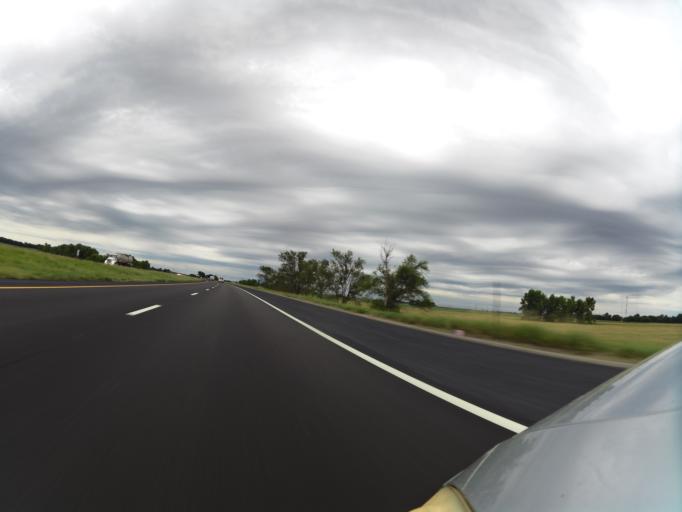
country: US
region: Kansas
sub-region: Sedgwick County
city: Maize
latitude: 37.8043
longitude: -97.4960
